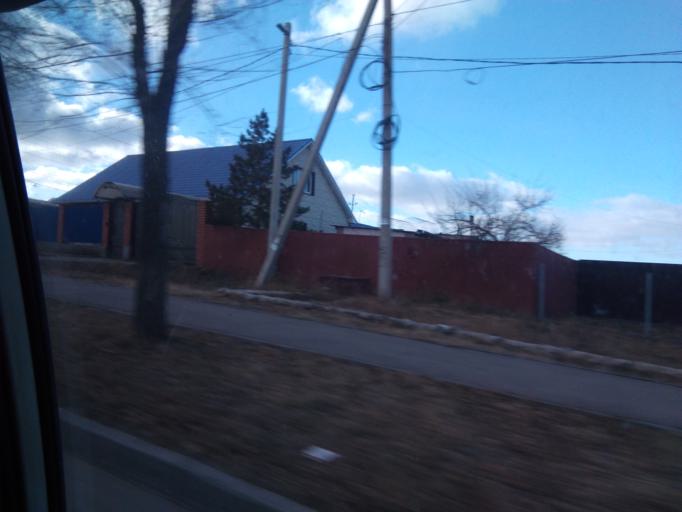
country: RU
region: Chelyabinsk
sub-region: Gorod Magnitogorsk
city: Magnitogorsk
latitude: 53.3886
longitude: 59.0524
